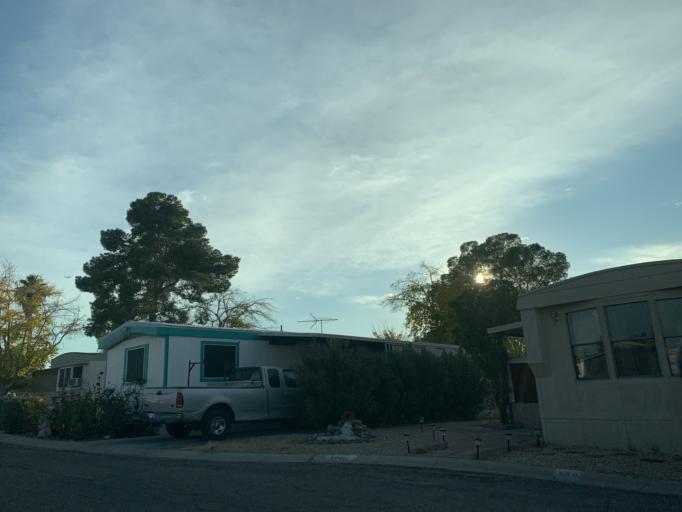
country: US
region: Nevada
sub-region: Clark County
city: Spring Valley
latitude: 36.1037
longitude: -115.2180
